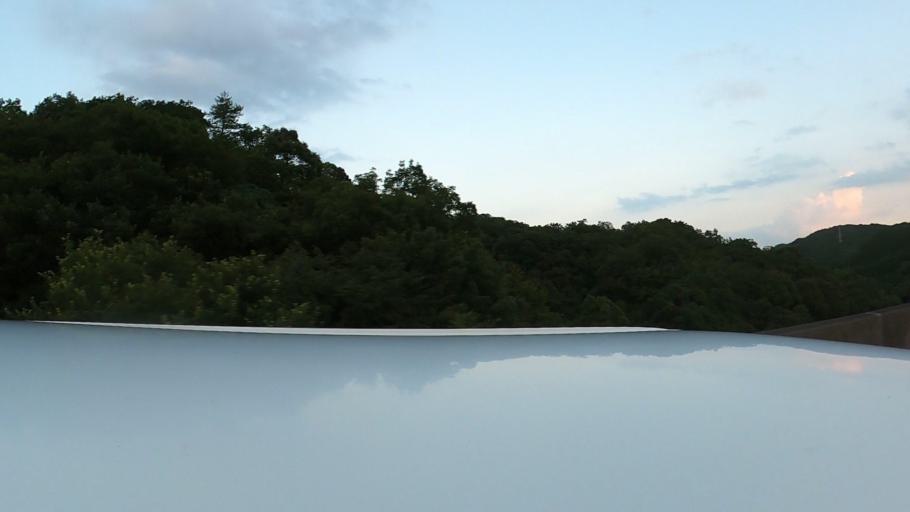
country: JP
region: Miyazaki
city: Nobeoka
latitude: 32.4569
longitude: 131.6140
